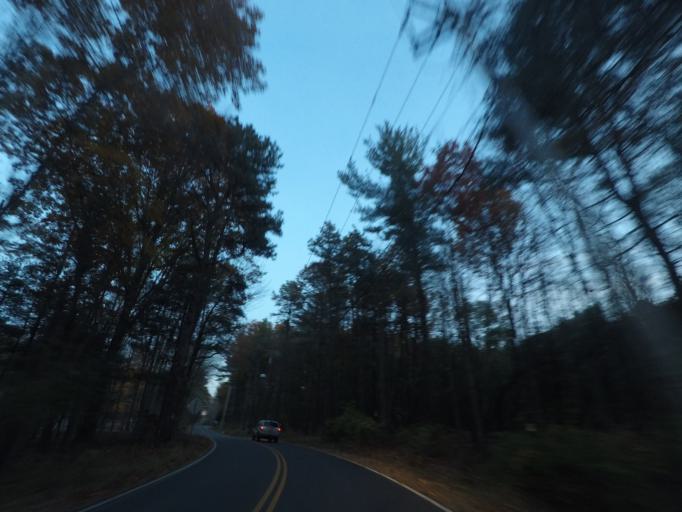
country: US
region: New York
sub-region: Albany County
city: Westmere
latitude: 42.7431
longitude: -73.9034
